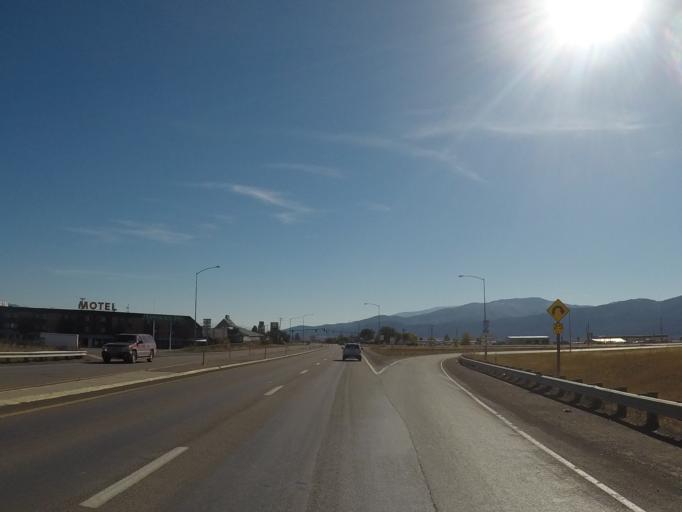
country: US
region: Montana
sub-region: Missoula County
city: Frenchtown
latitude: 46.9509
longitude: -114.1314
